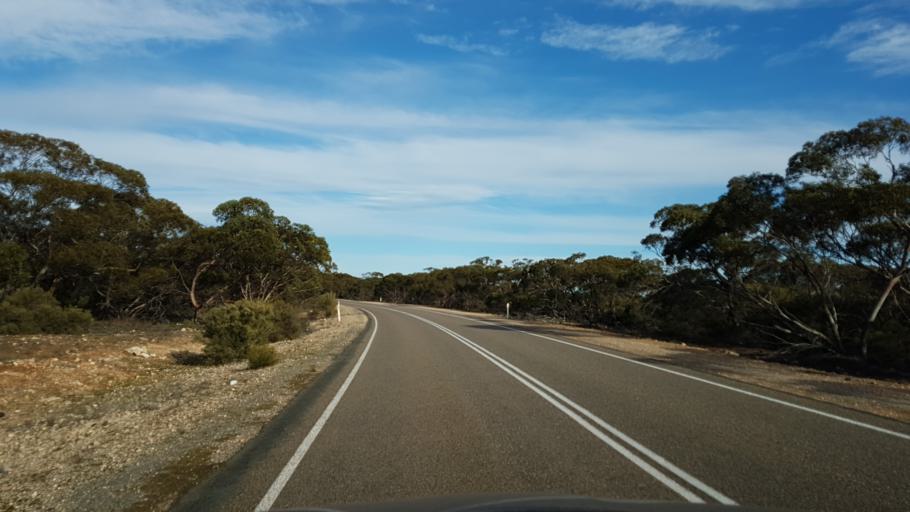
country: AU
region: South Australia
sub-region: Mid Murray
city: Mannum
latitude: -35.0078
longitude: 139.5271
